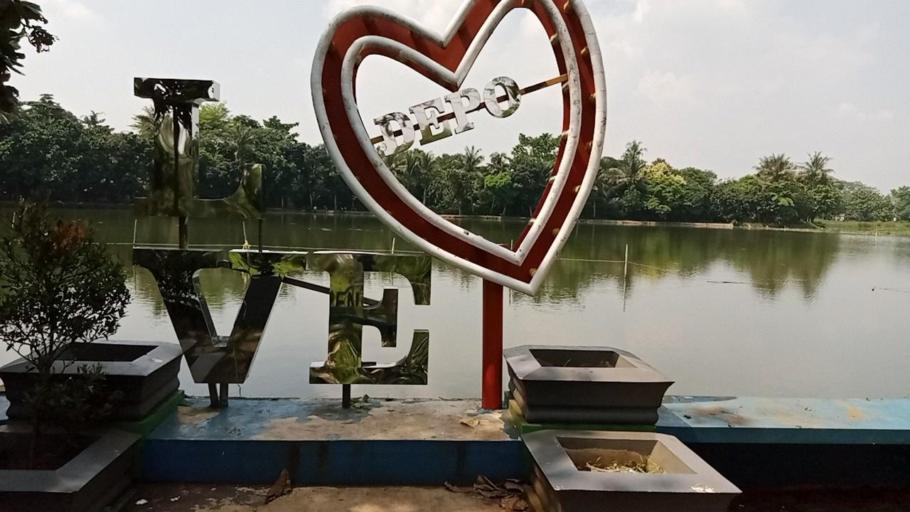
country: ID
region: West Java
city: Parung
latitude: -6.4206
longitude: 106.7490
